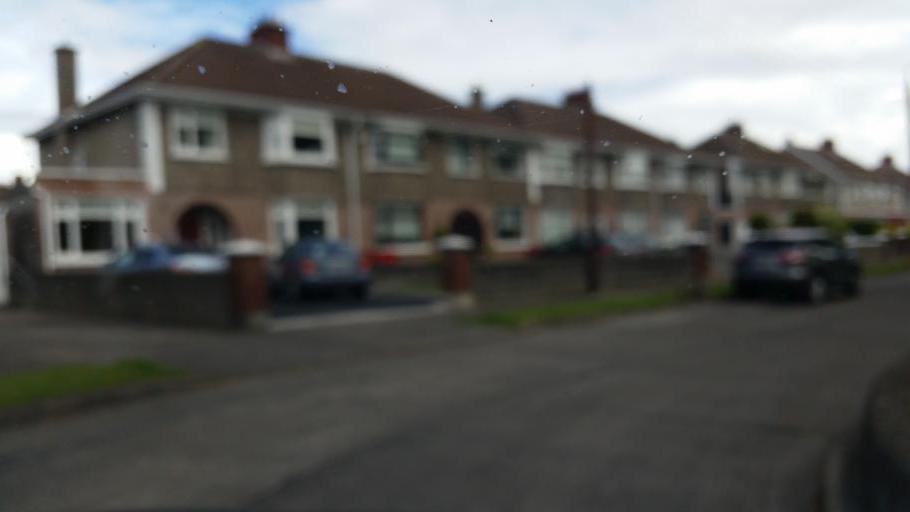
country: IE
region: Leinster
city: Ballymun
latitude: 53.3925
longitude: -6.2753
